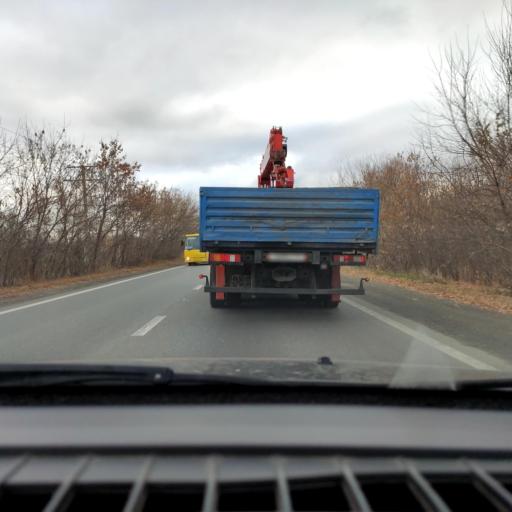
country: RU
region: Samara
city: Tol'yatti
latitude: 53.5582
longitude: 49.3614
